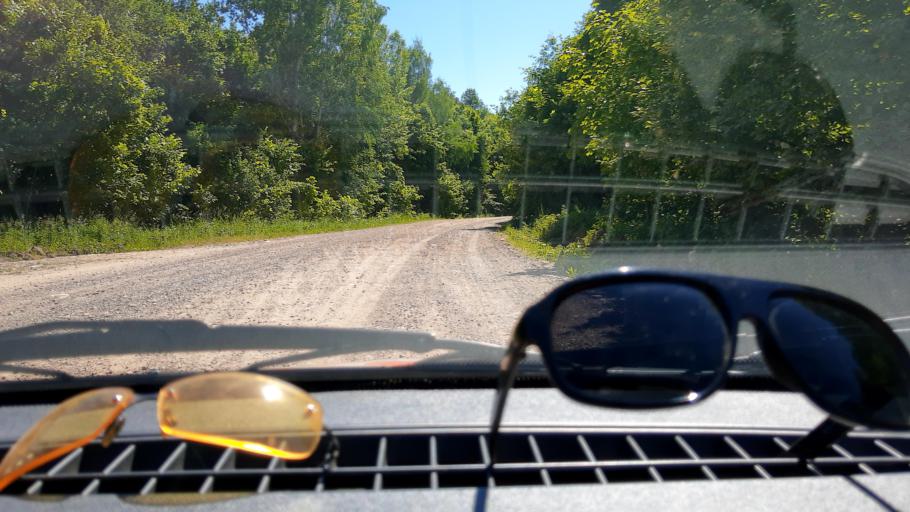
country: RU
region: Bashkortostan
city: Ulu-Telyak
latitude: 54.8023
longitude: 57.0322
